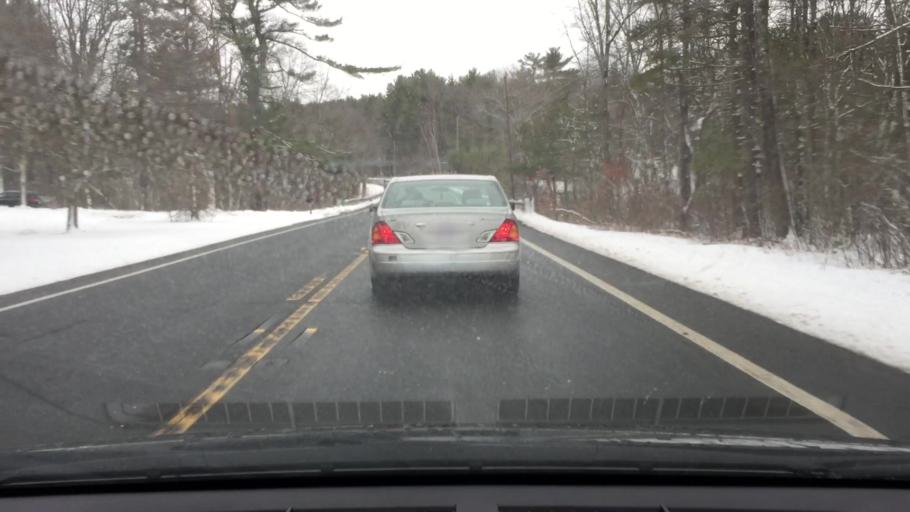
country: US
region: Massachusetts
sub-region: Hampshire County
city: Pelham
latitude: 42.3500
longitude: -72.4037
